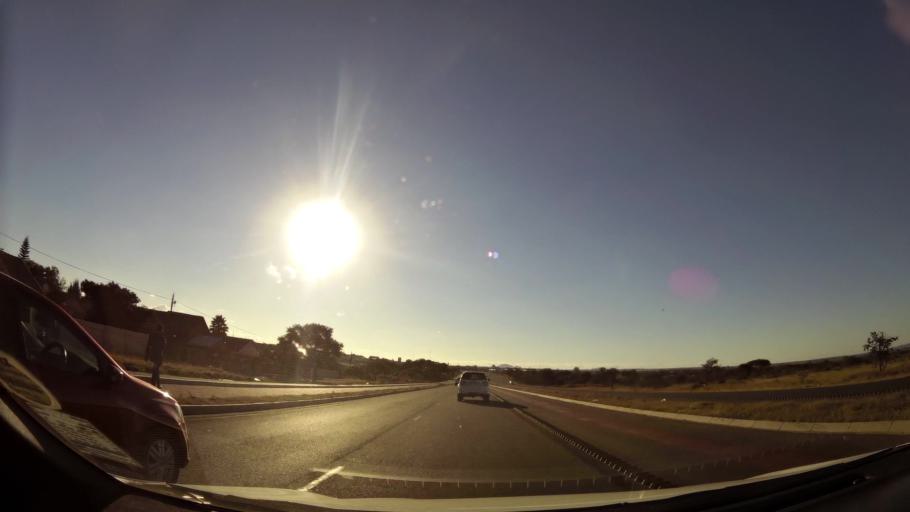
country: ZA
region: Limpopo
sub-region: Capricorn District Municipality
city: Polokwane
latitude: -23.8596
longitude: 29.4040
